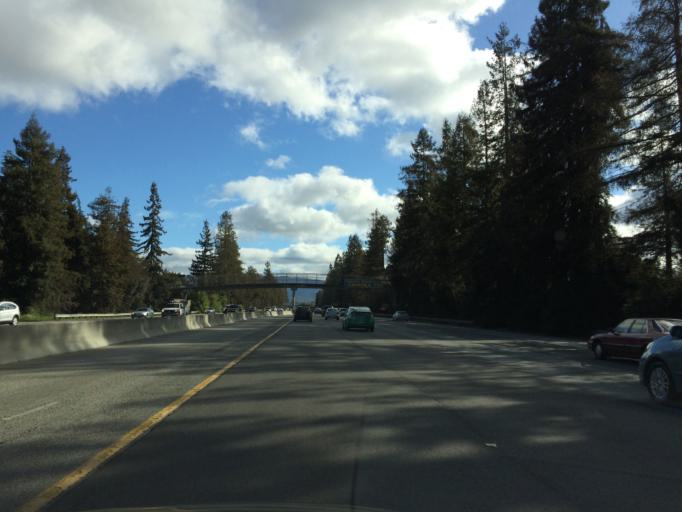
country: US
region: California
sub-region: Santa Clara County
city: Burbank
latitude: 37.3067
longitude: -121.9407
